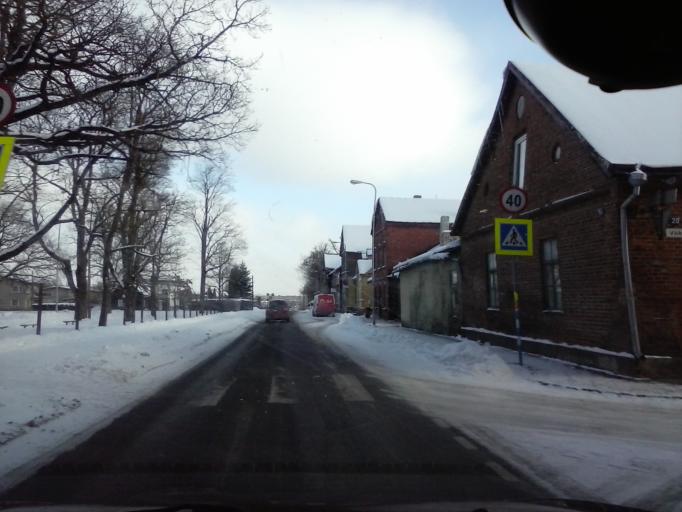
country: EE
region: Viljandimaa
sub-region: Viljandi linn
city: Viljandi
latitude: 58.3659
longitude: 25.6088
